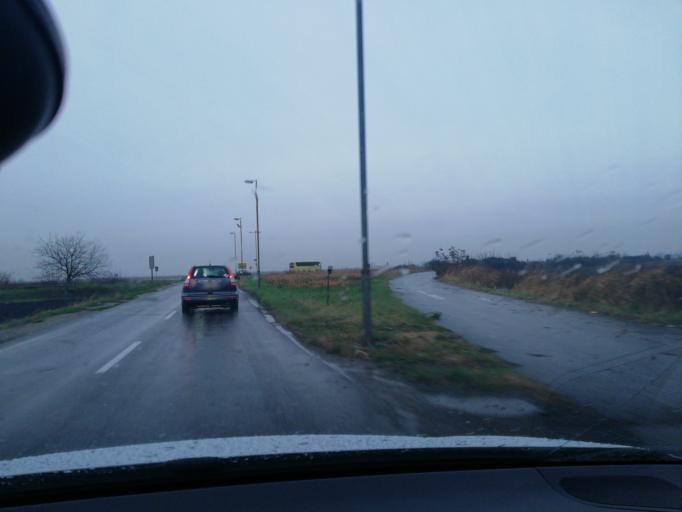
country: RS
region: Autonomna Pokrajina Vojvodina
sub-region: Sremski Okrug
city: Ruma
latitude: 44.9846
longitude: 19.8186
